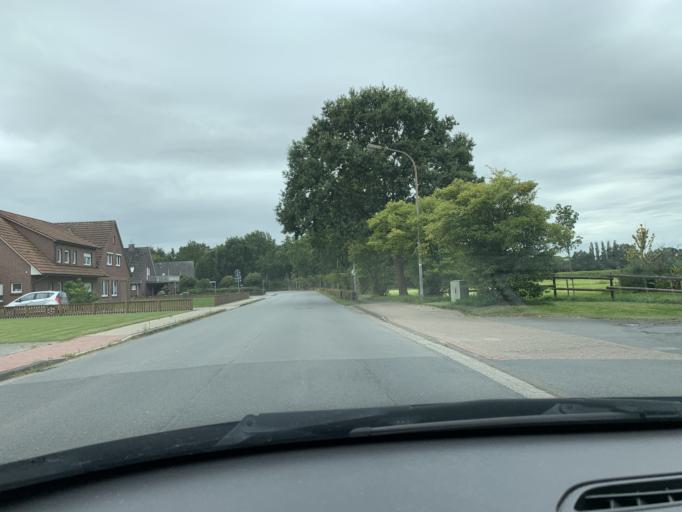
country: DE
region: Lower Saxony
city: Westerstede
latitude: 53.3132
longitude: 7.9189
